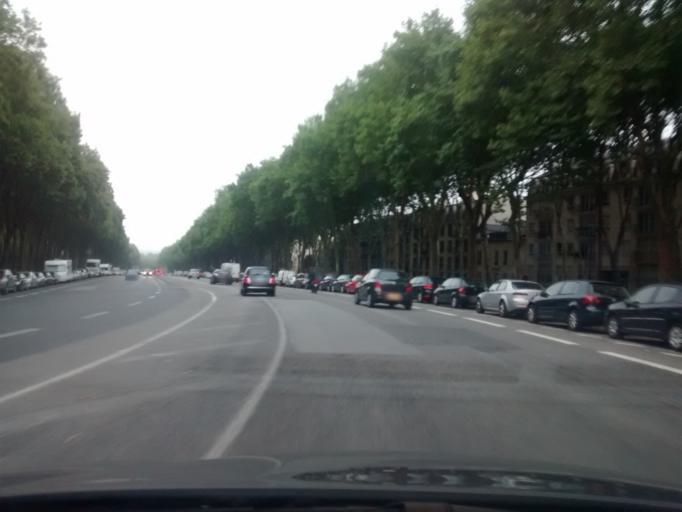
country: FR
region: Ile-de-France
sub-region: Departement des Yvelines
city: Versailles
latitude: 48.7982
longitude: 2.1449
